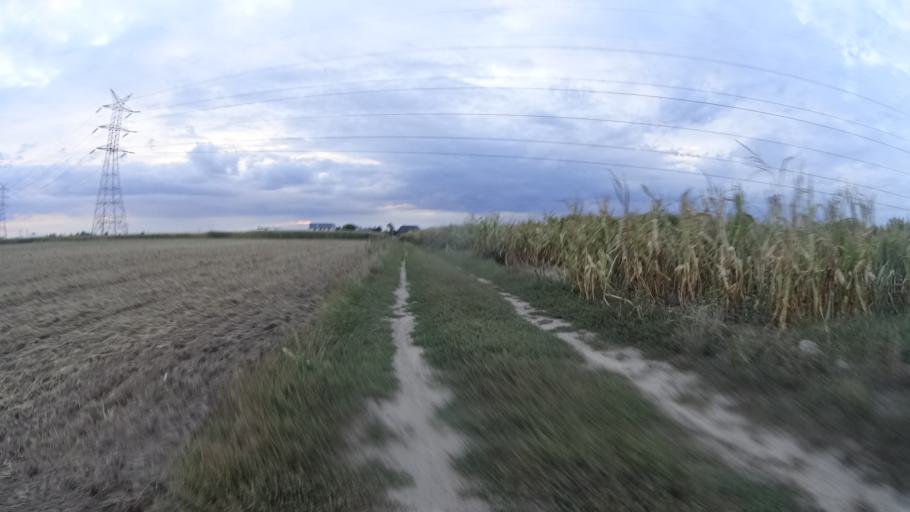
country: PL
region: Masovian Voivodeship
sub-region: Powiat warszawski zachodni
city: Ozarow Mazowiecki
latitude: 52.2405
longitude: 20.7705
